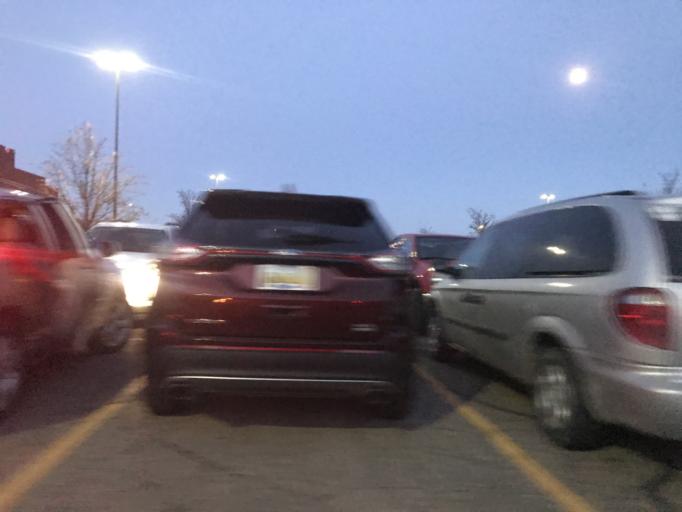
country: US
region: Michigan
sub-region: Livingston County
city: Brighton
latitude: 42.5476
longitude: -83.7996
